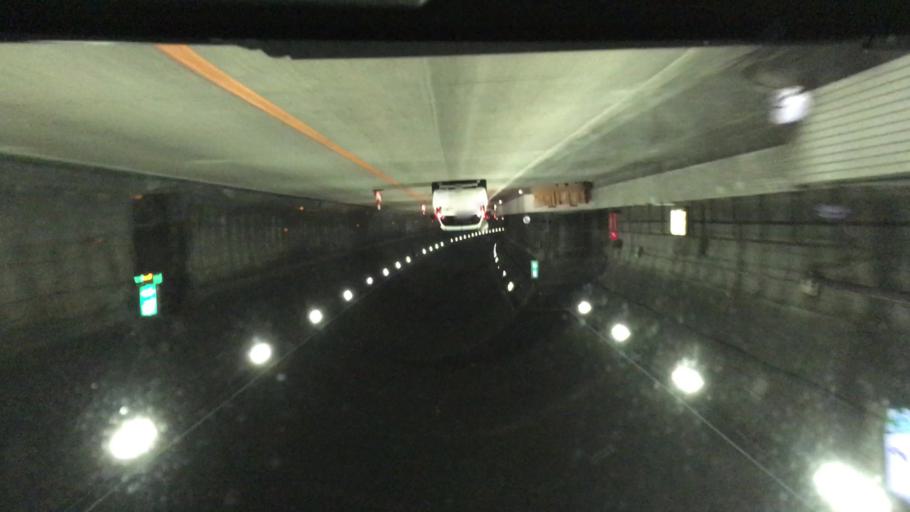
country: JP
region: Yamaguchi
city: Tokuyama
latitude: 34.0906
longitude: 131.7721
